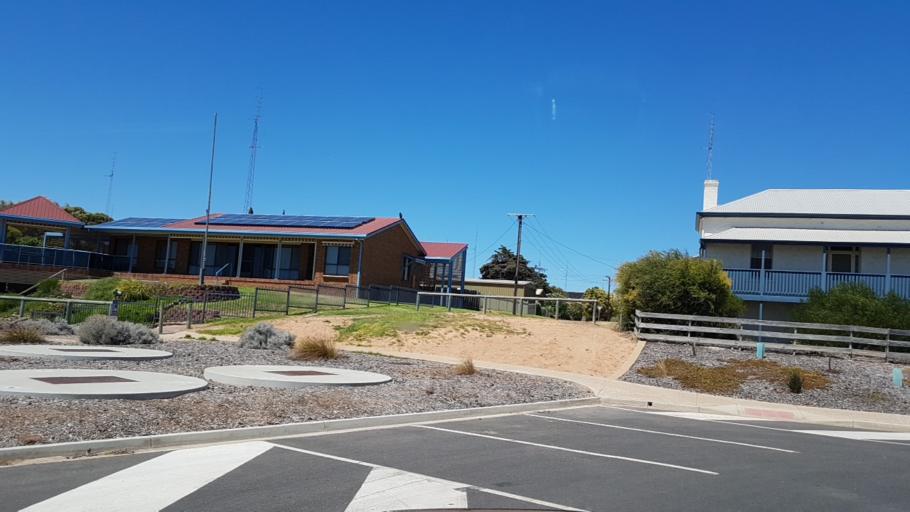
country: AU
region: South Australia
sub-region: Copper Coast
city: Wallaroo
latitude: -34.0582
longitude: 137.5597
